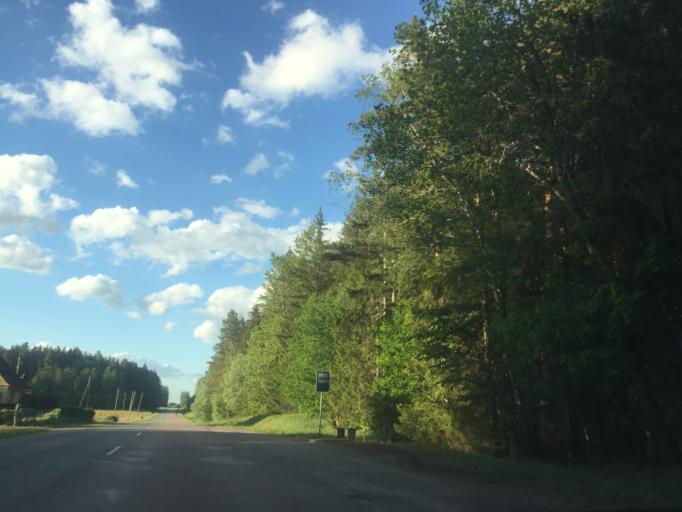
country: LV
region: Kandava
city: Kandava
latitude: 57.0081
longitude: 22.7826
